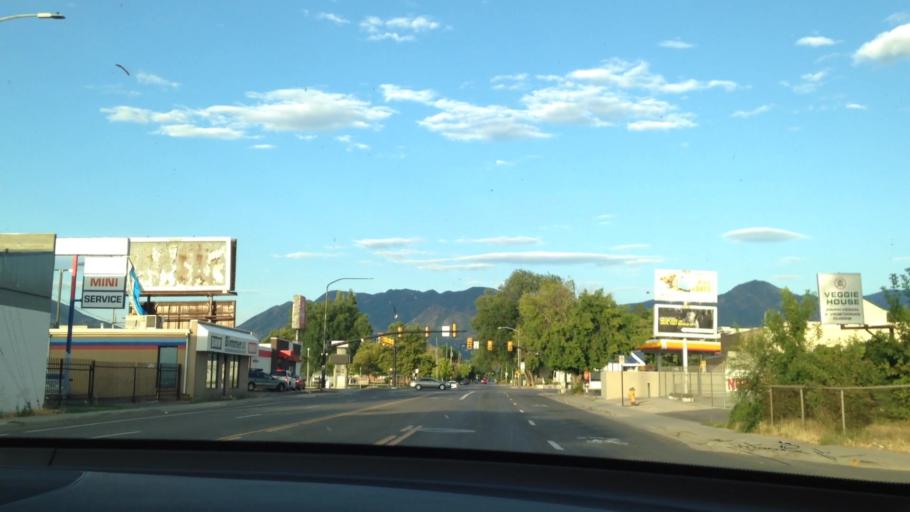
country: US
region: Utah
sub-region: Salt Lake County
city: South Salt Lake
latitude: 40.7335
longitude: -111.8898
